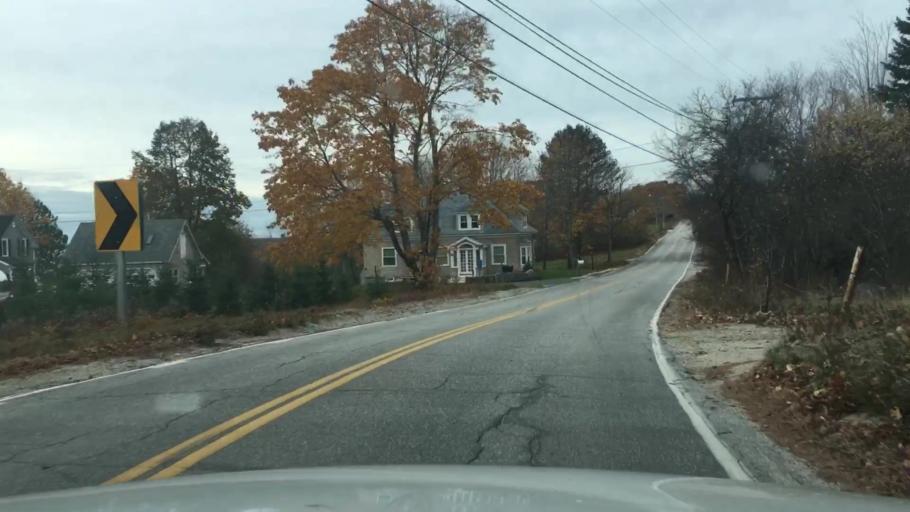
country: US
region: Maine
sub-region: Hancock County
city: Sedgwick
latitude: 44.3546
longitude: -68.5490
